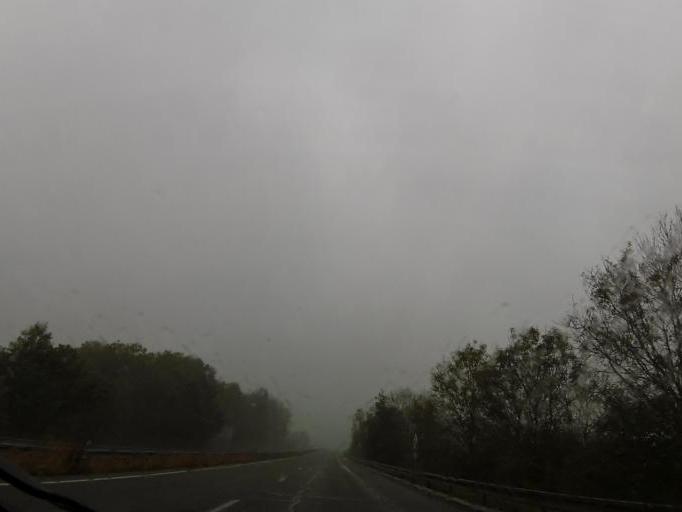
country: FR
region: Picardie
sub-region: Departement de l'Aisne
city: Charly-sur-Marne
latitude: 49.0473
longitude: 3.2844
